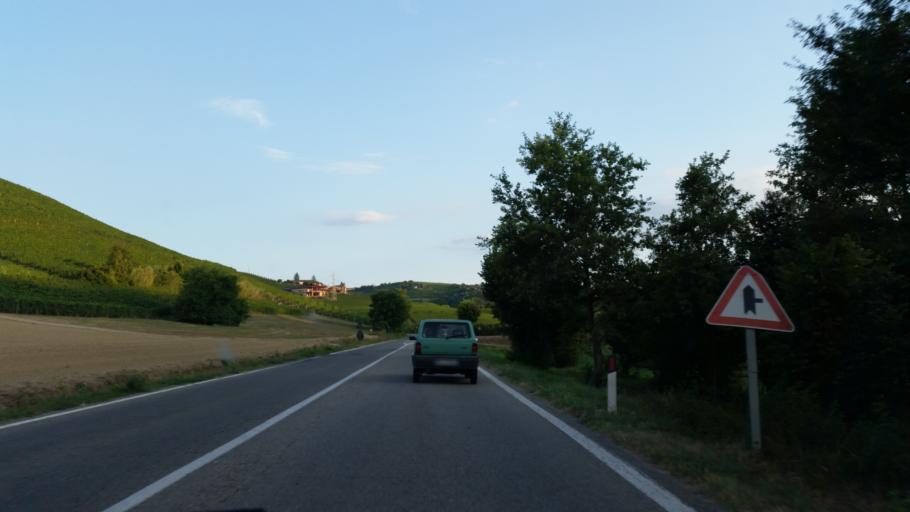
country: IT
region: Piedmont
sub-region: Provincia di Cuneo
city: Barbaresco
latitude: 44.7319
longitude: 8.0942
